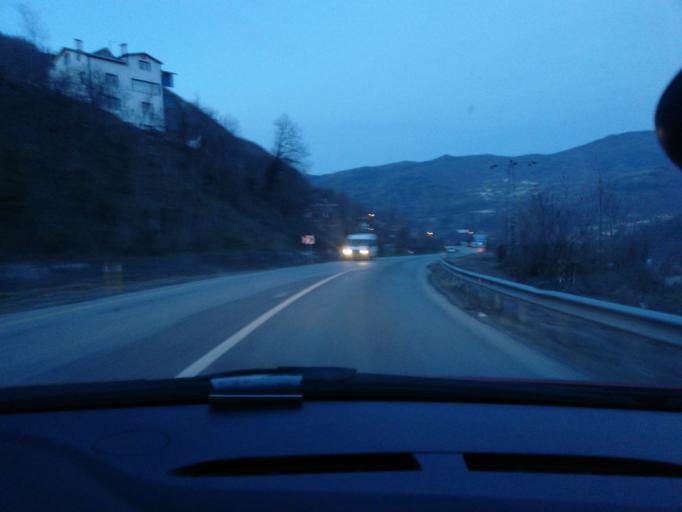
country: TR
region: Kastamonu
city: Inebolu
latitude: 41.9370
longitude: 33.7542
